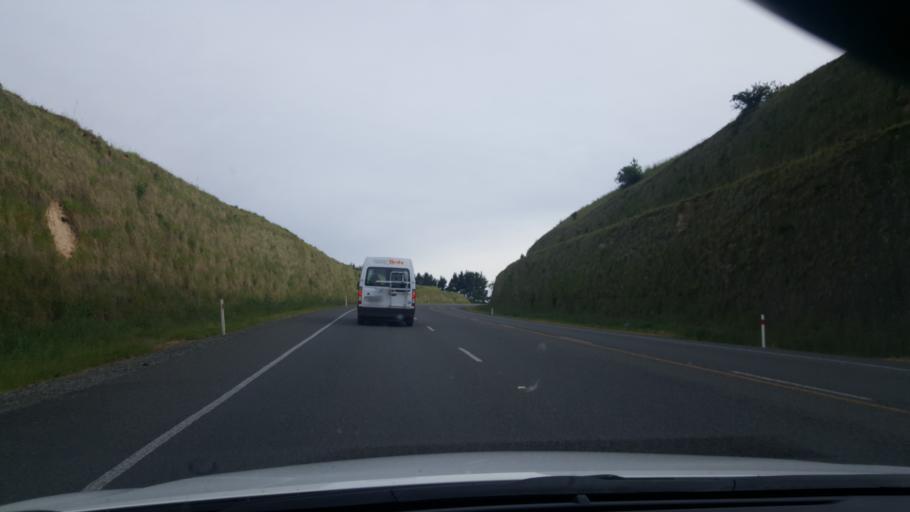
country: NZ
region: Waikato
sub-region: Taupo District
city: Taupo
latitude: -38.6397
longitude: 176.0983
